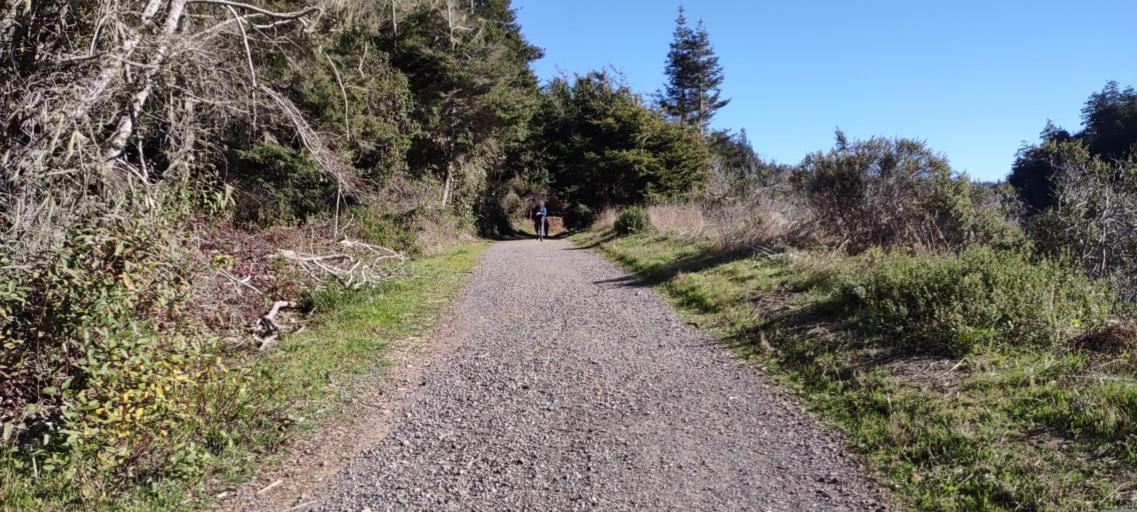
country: US
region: California
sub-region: Mendocino County
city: Fort Bragg
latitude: 39.3041
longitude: -123.7833
